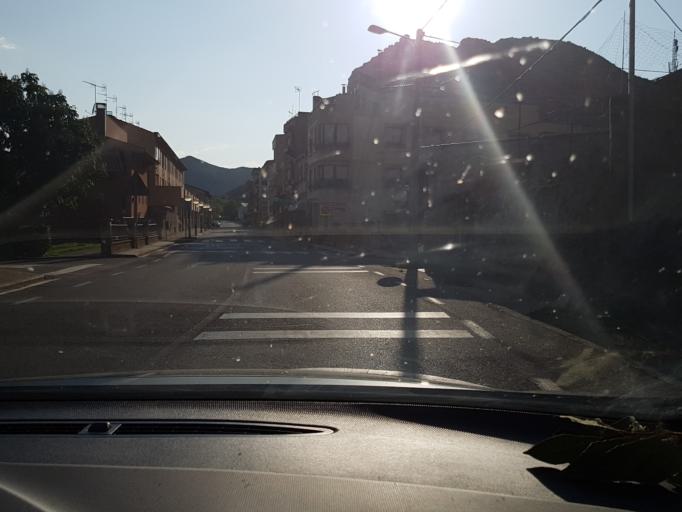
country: ES
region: La Rioja
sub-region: Provincia de La Rioja
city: Herce
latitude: 42.2140
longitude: -2.1639
